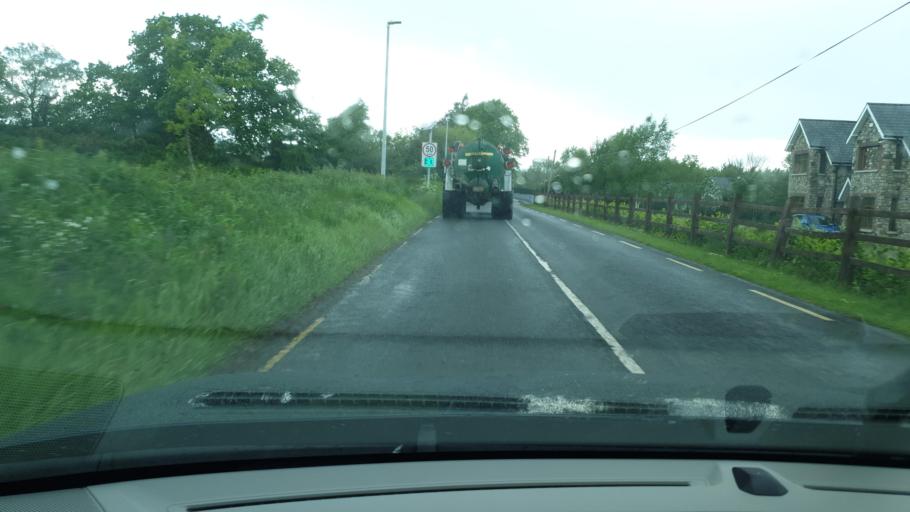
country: IE
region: Leinster
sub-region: Laois
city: Mountrath
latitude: 53.0547
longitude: -7.4066
